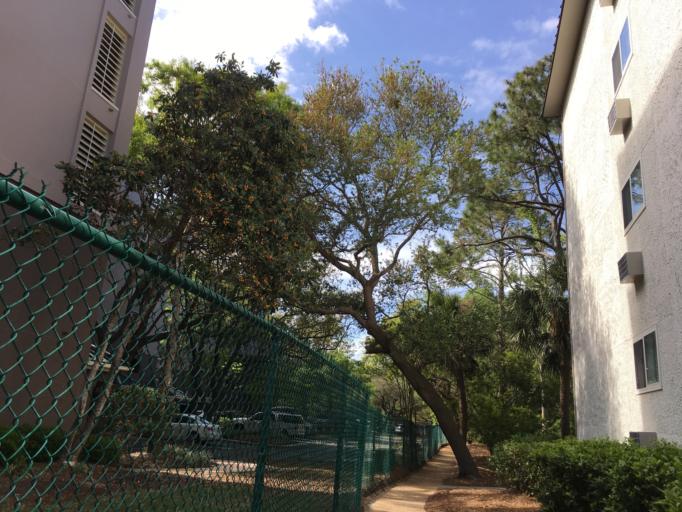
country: US
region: South Carolina
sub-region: Beaufort County
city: Hilton Head Island
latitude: 32.1373
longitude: -80.7604
